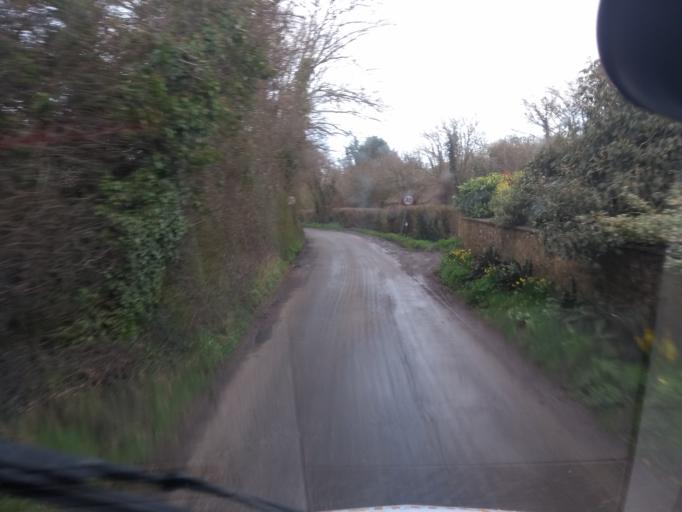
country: GB
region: England
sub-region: Somerset
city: South Petherton
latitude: 50.9792
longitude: -2.8246
